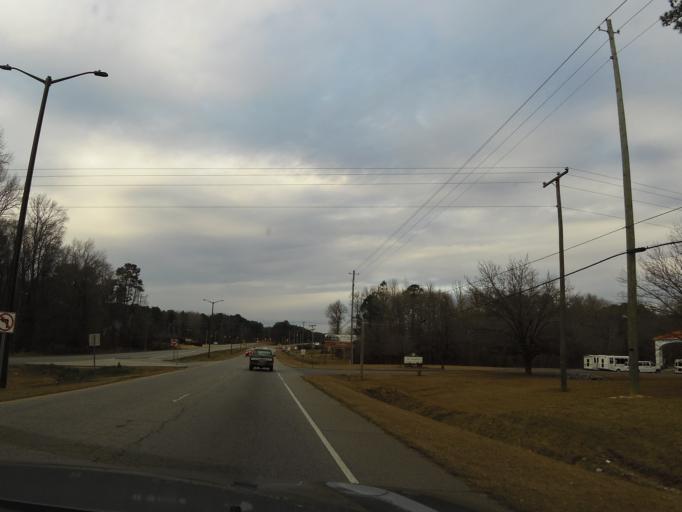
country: US
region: North Carolina
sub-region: Nash County
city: Rocky Mount
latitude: 36.0298
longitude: -77.7670
